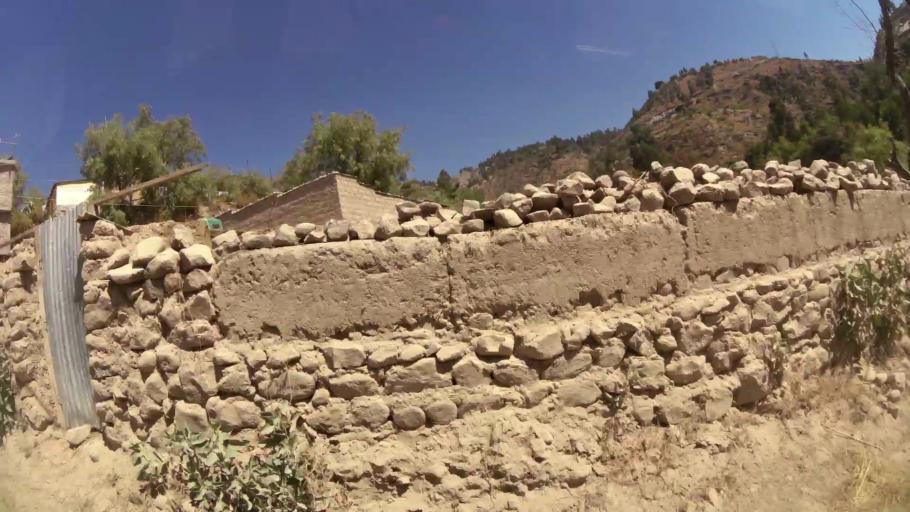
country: PE
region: Ayacucho
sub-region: Provincia de Huamanga
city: Ayacucho
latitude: -13.1695
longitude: -74.2367
